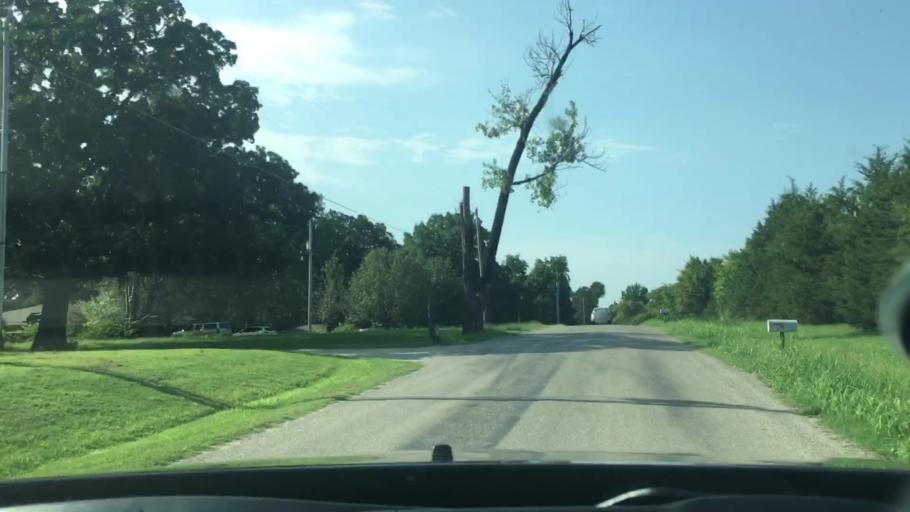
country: US
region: Oklahoma
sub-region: Johnston County
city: Tishomingo
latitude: 34.2206
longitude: -96.6711
